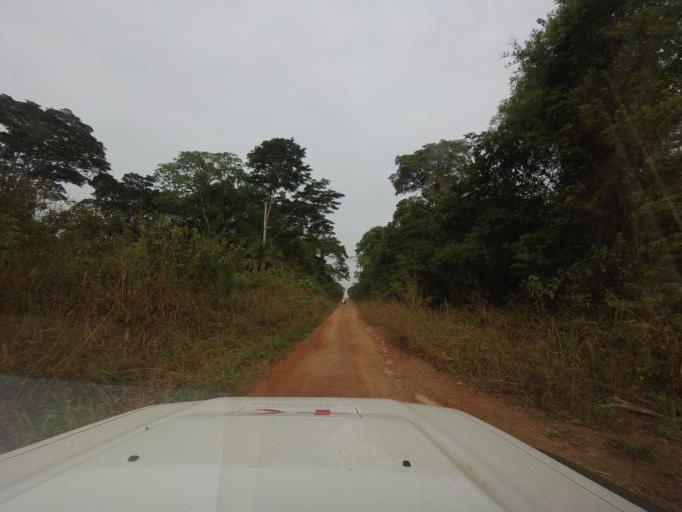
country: LR
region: Lofa
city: Voinjama
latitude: 8.3756
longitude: -9.8741
